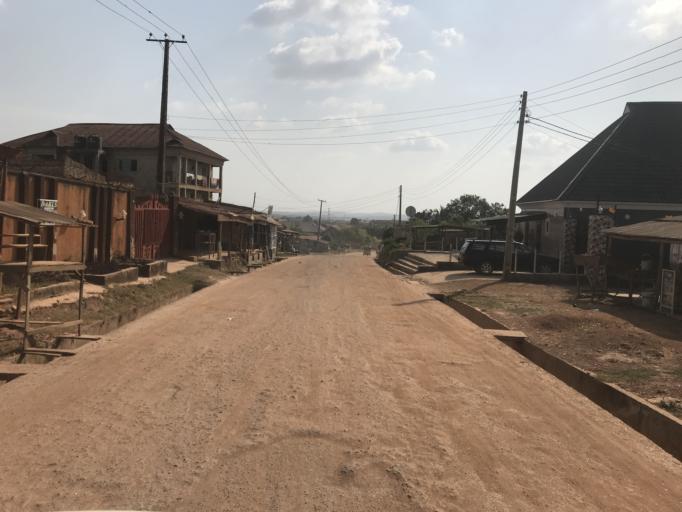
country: NG
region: Osun
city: Osogbo
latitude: 7.8074
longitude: 4.5579
